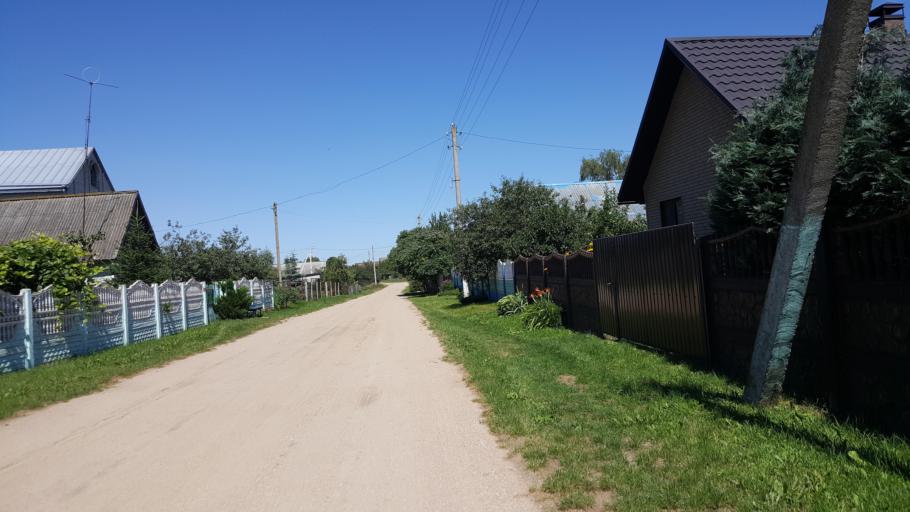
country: BY
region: Brest
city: Charnawchytsy
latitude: 52.2317
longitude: 23.7794
